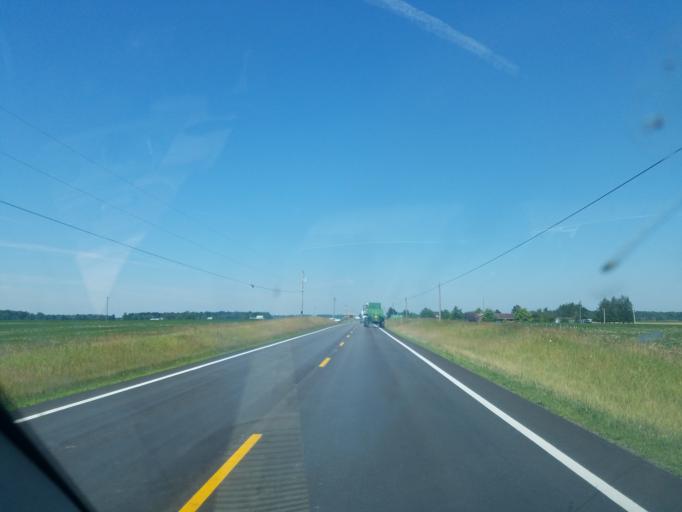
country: US
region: Ohio
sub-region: Shelby County
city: Botkins
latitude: 40.4391
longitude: -84.1188
